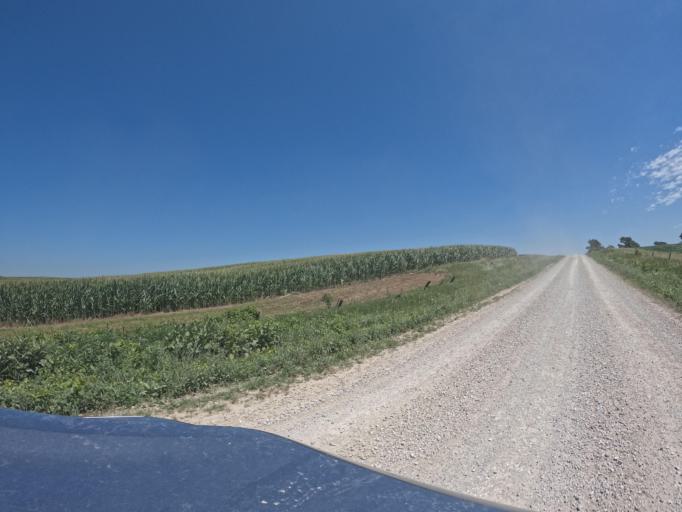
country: US
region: Iowa
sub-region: Keokuk County
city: Sigourney
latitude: 41.4523
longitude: -92.3587
